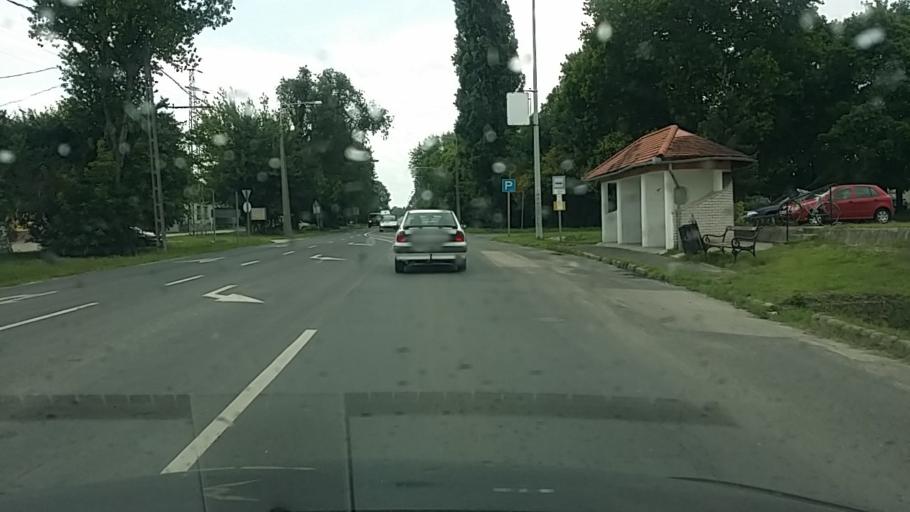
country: HU
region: Pest
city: Orkeny
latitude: 47.1274
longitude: 19.4279
